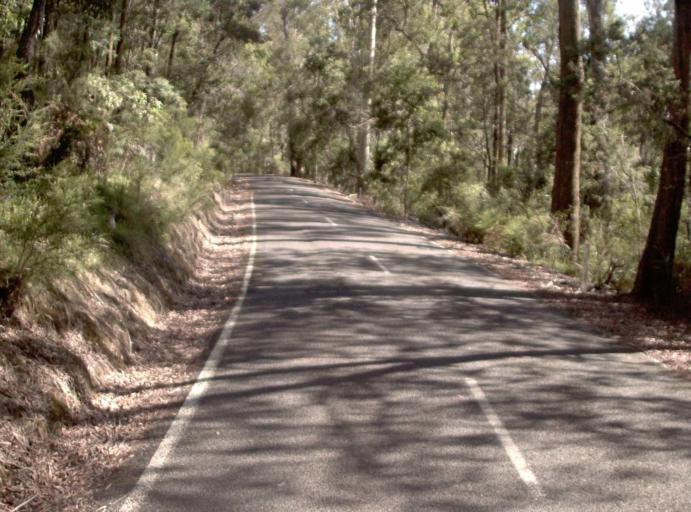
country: AU
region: New South Wales
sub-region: Bombala
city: Bombala
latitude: -37.3758
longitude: 148.6816
